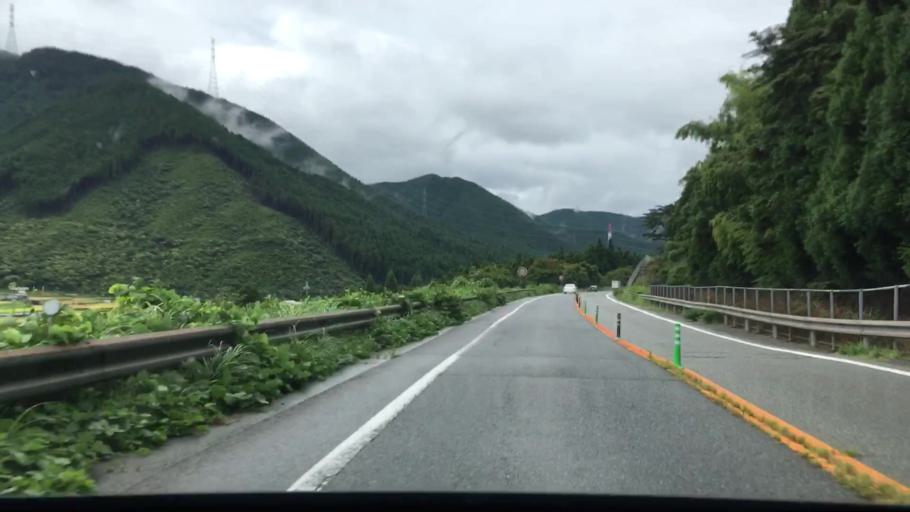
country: JP
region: Hyogo
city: Nishiwaki
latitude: 35.1299
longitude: 134.7880
